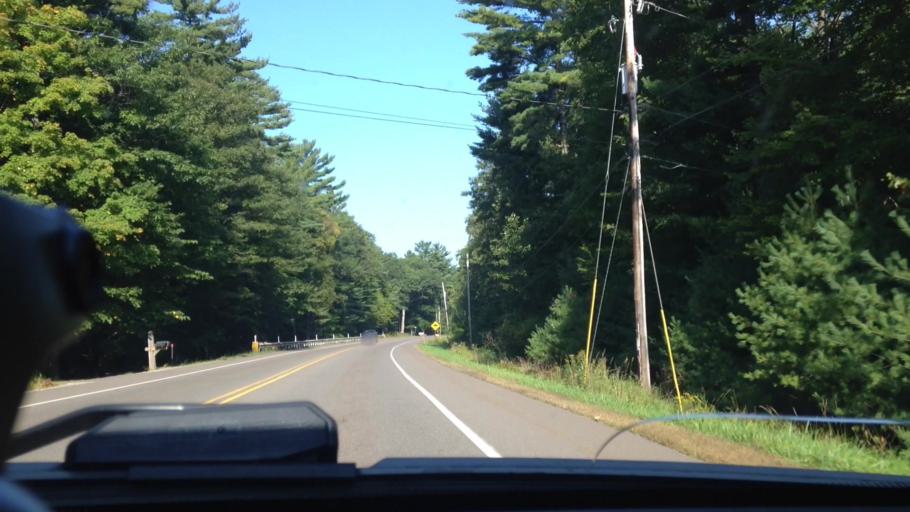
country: US
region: Michigan
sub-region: Dickinson County
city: Quinnesec
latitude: 45.8318
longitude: -88.0031
